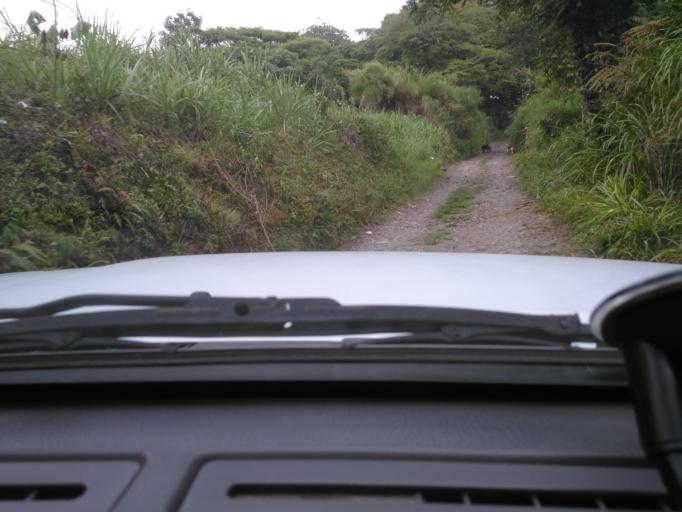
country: MX
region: Veracruz
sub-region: Mariano Escobedo
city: Chicola
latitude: 18.8951
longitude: -97.1089
